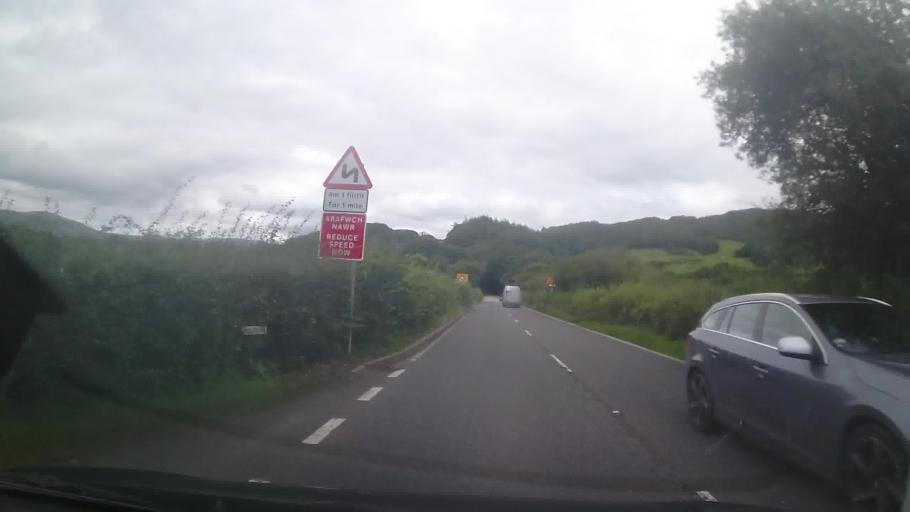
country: GB
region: Wales
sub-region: Sir Powys
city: Machynlleth
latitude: 52.5611
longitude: -3.9139
